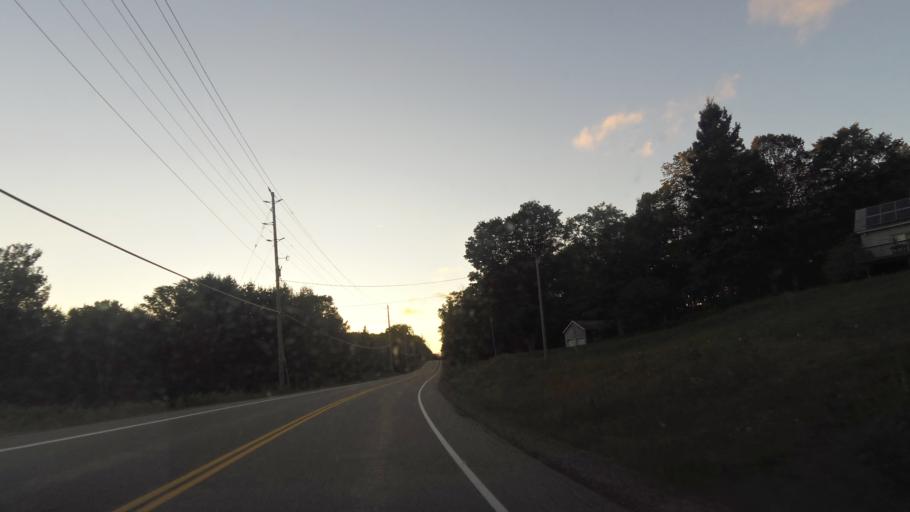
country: CA
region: Ontario
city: Bancroft
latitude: 45.0283
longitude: -78.4011
